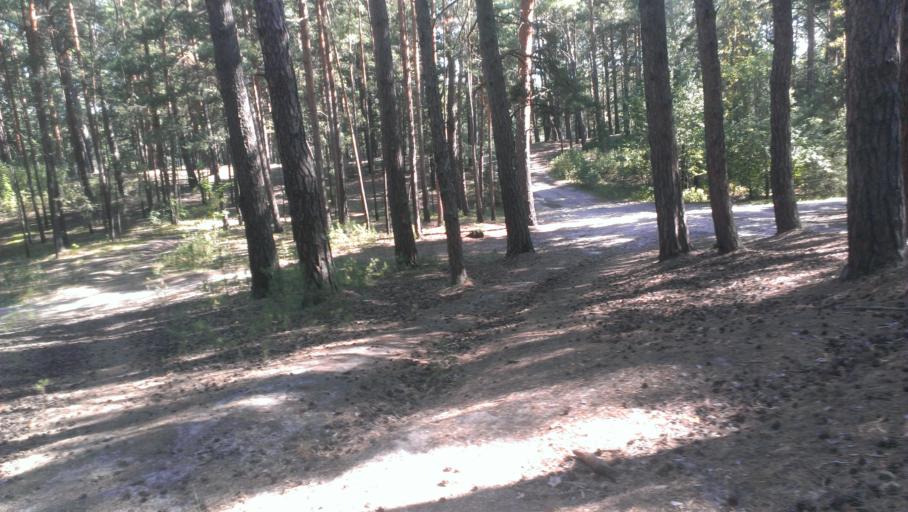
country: RU
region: Altai Krai
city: Yuzhnyy
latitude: 53.3162
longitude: 83.6888
